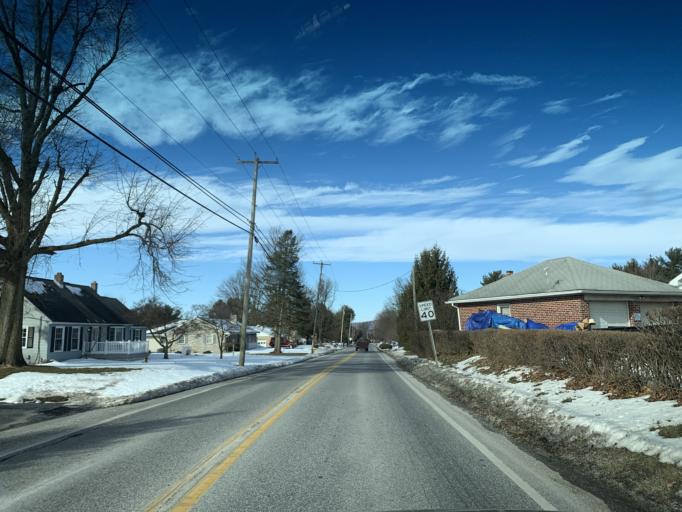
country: US
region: Pennsylvania
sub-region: York County
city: Dover
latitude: 39.9736
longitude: -76.8494
